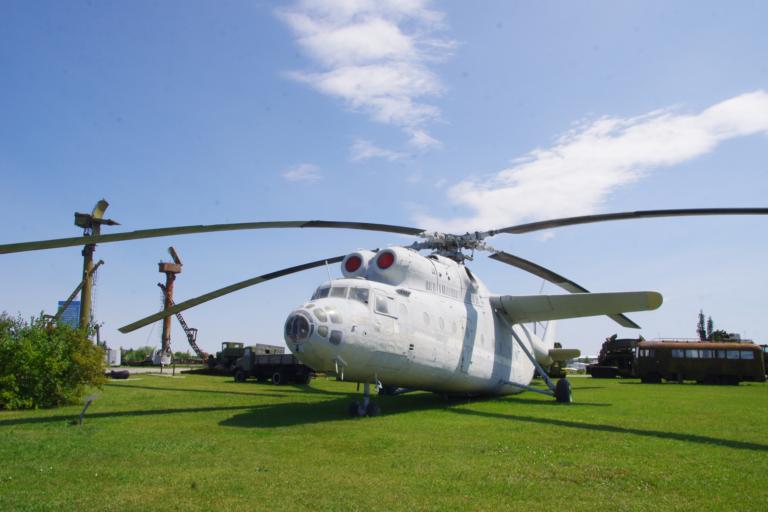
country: RU
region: Samara
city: Tol'yatti
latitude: 53.5522
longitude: 49.2497
